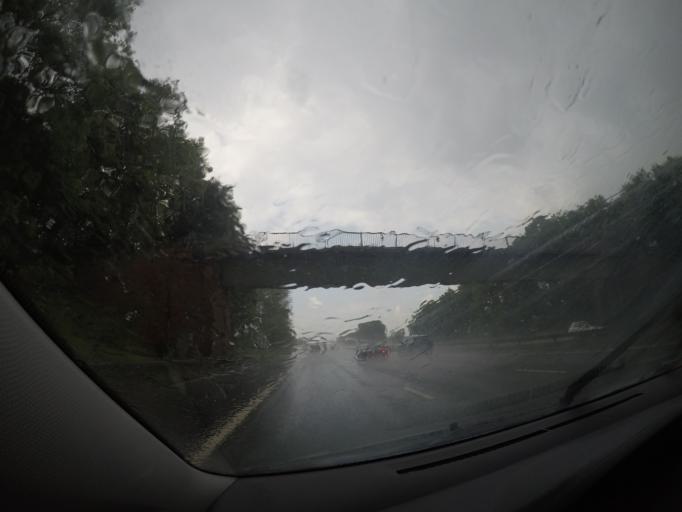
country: GB
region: England
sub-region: Cumbria
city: Penrith
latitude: 54.7147
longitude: -2.7965
